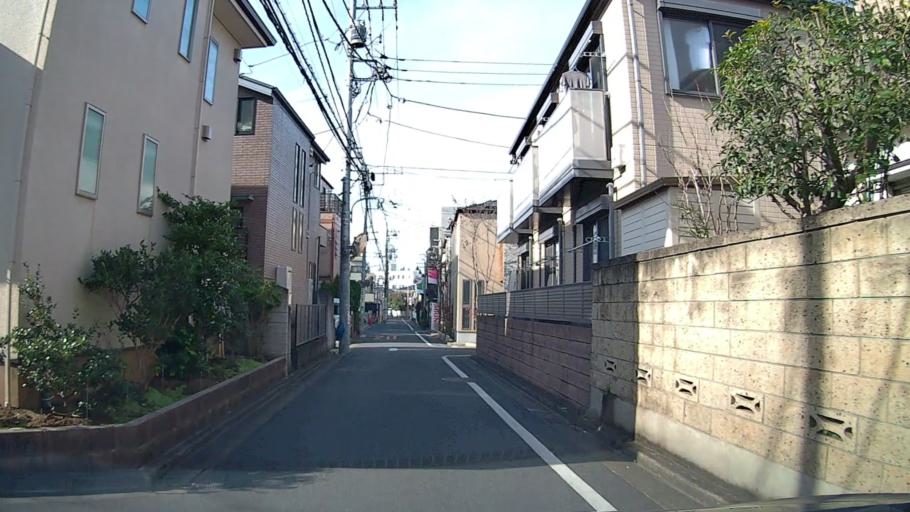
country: JP
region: Saitama
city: Wako
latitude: 35.7350
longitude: 139.6198
